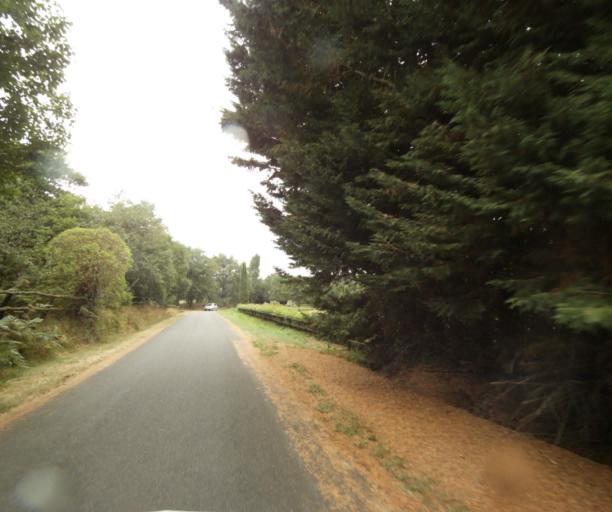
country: FR
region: Pays de la Loire
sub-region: Departement de la Sarthe
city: Sable-sur-Sarthe
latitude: 47.8206
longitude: -0.3668
